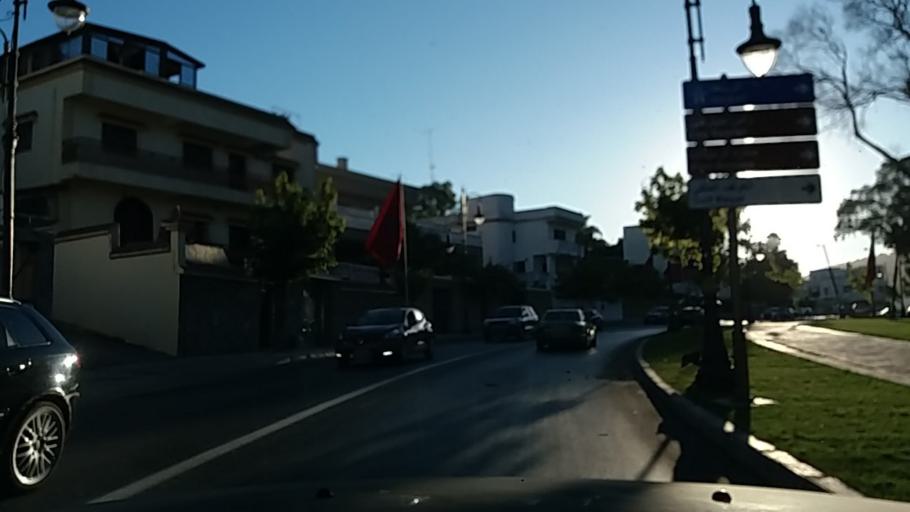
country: MA
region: Tanger-Tetouan
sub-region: Tanger-Assilah
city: Tangier
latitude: 35.7785
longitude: -5.8327
